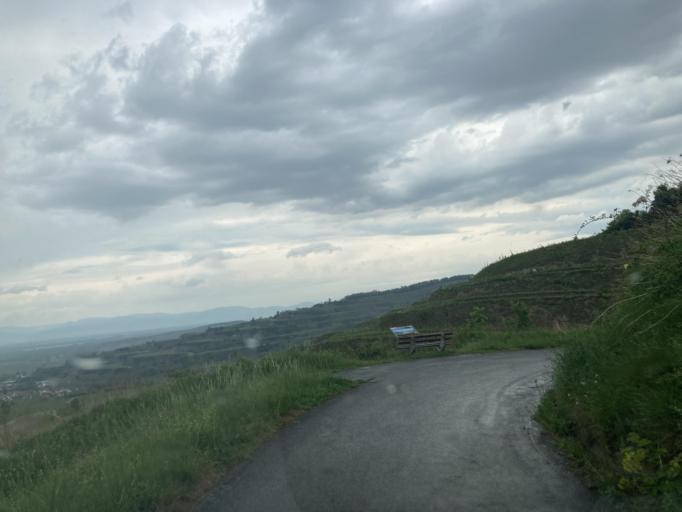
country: DE
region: Baden-Wuerttemberg
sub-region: Freiburg Region
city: Vogtsburg
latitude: 48.0870
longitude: 7.6583
